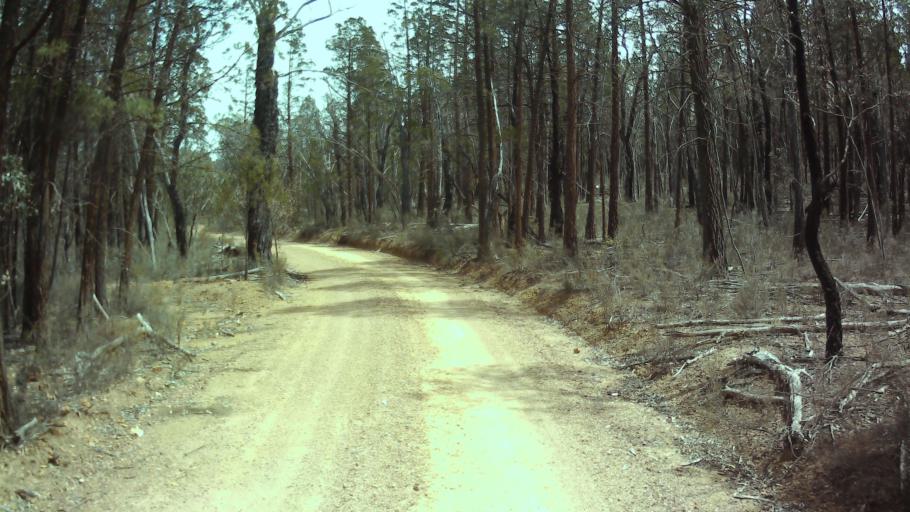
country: AU
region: New South Wales
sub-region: Weddin
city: Grenfell
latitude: -33.8902
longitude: 148.3867
